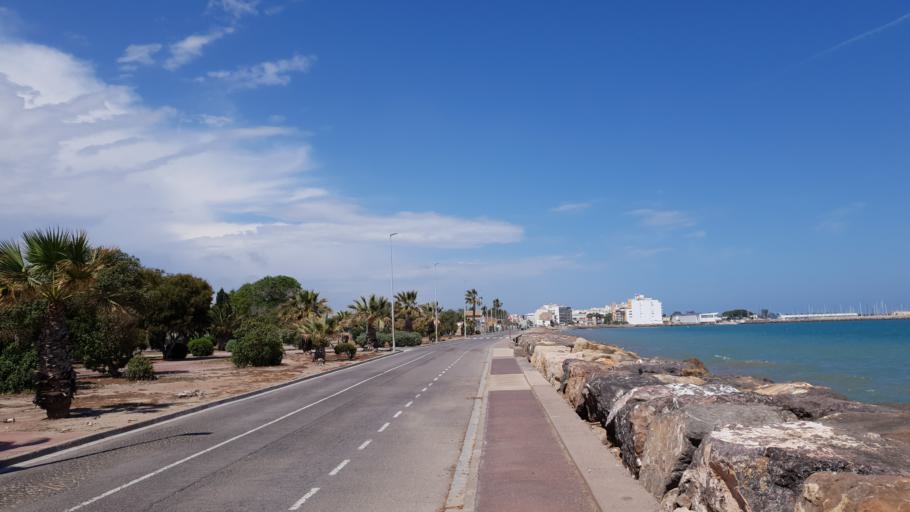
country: ES
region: Valencia
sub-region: Provincia de Castello
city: Burriana
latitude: 39.8586
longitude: -0.0837
